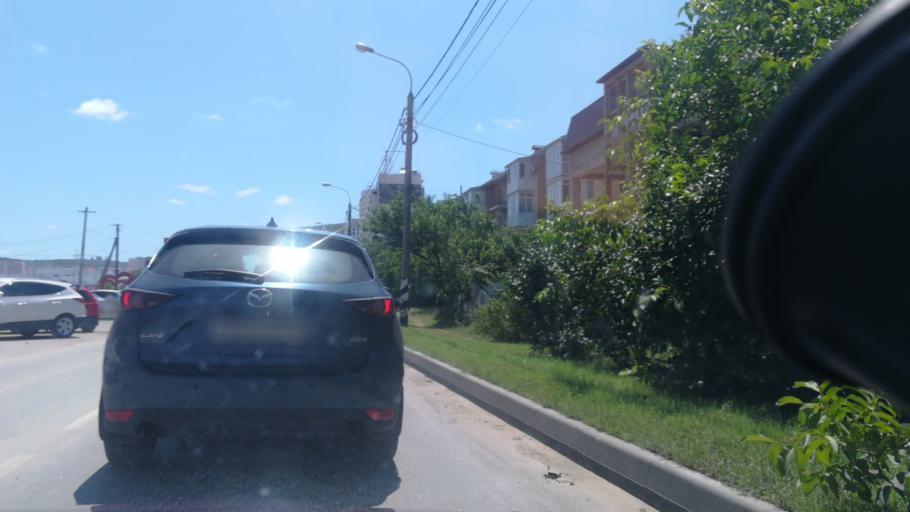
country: RU
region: Krasnodarskiy
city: Anapa
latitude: 44.8839
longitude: 37.3381
